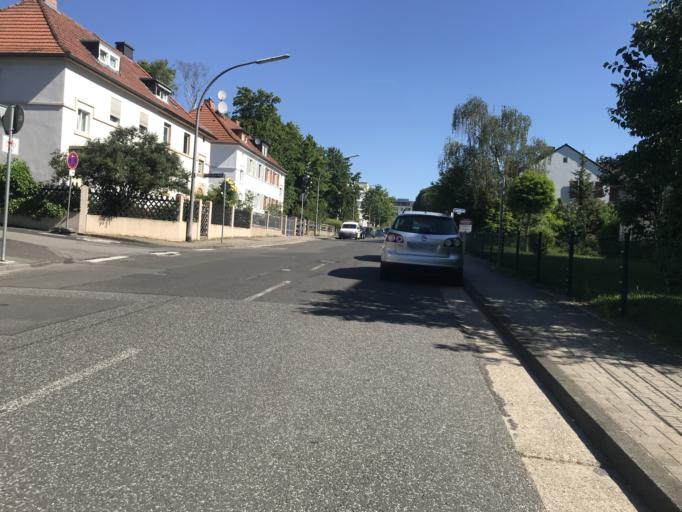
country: DE
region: Rheinland-Pfalz
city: Budenheim
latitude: 50.0522
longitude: 8.1973
